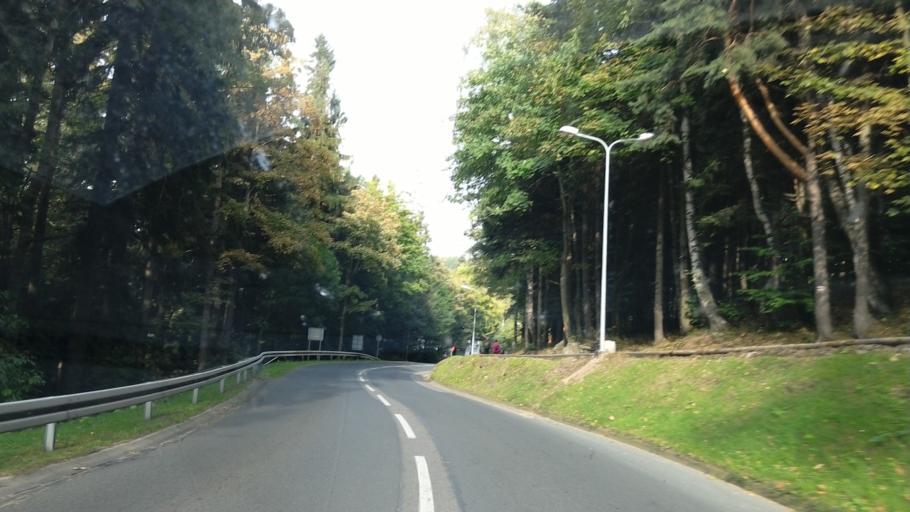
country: PL
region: Lower Silesian Voivodeship
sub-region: Powiat jeleniogorski
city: Karpacz
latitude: 50.7752
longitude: 15.7407
